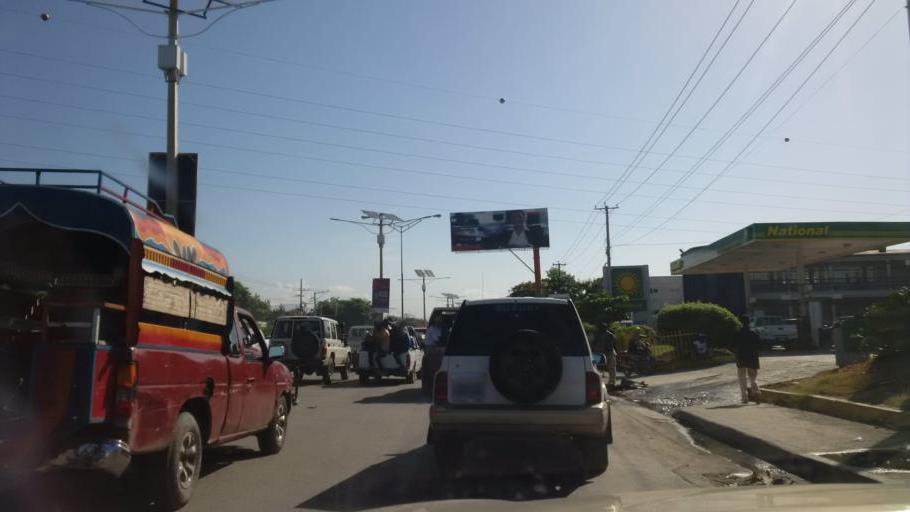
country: HT
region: Ouest
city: Delmas 73
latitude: 18.5657
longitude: -72.3133
